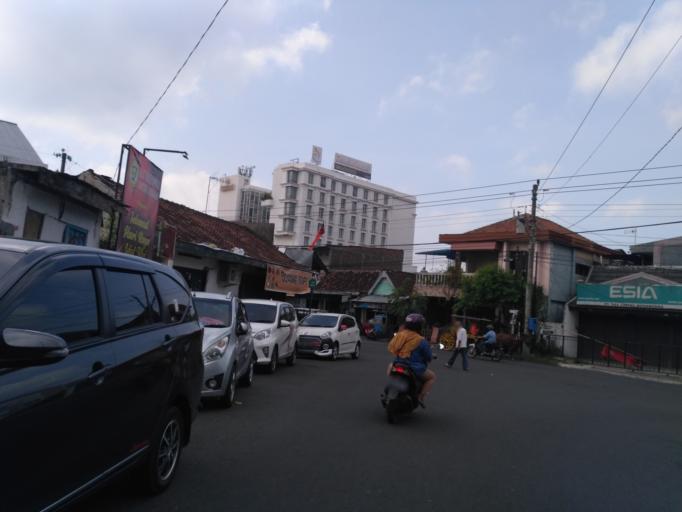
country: ID
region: Daerah Istimewa Yogyakarta
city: Yogyakarta
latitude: -7.7965
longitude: 110.3713
